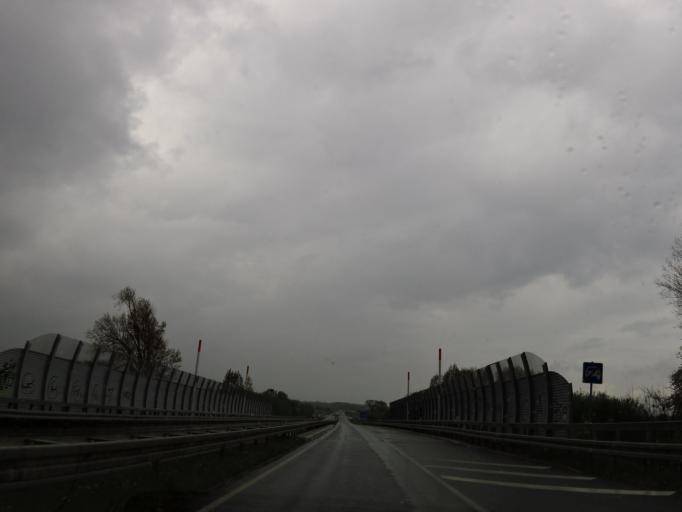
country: NL
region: Limburg
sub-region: Gemeente Sittard-Geleen
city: Sittard
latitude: 51.0318
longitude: 5.8777
